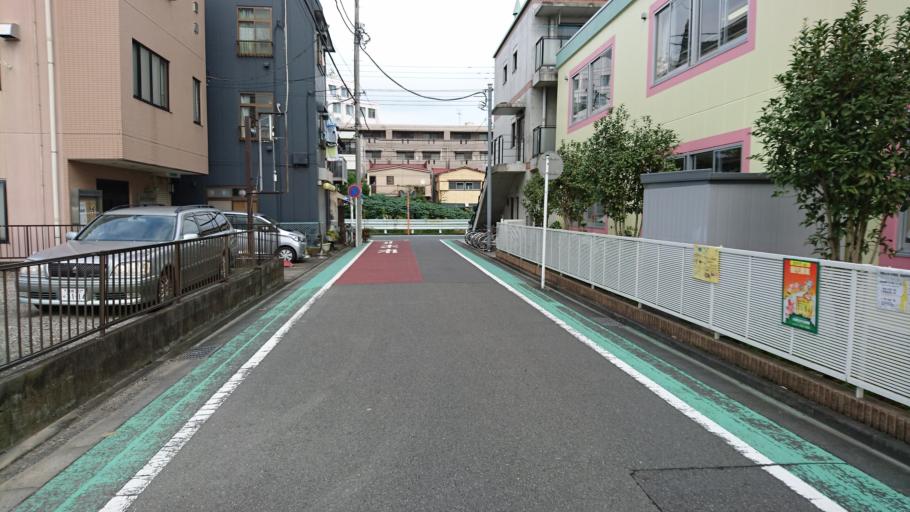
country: JP
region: Tokyo
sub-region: Machida-shi
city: Machida
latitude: 35.5717
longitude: 139.3883
